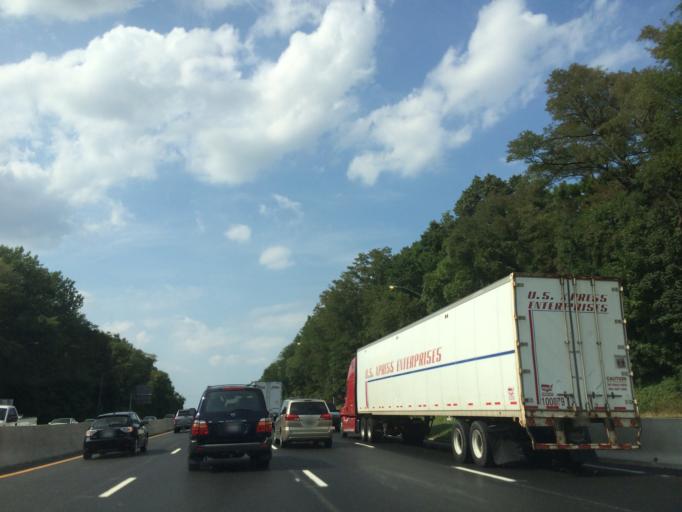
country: US
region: Maryland
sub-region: Baltimore County
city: Catonsville
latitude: 39.2742
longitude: -76.7244
